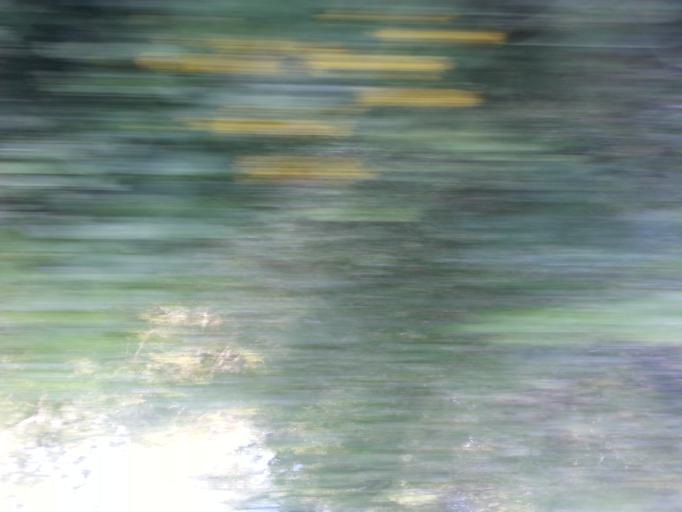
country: US
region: Tennessee
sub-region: Knox County
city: Knoxville
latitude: 35.8919
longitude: -83.8729
